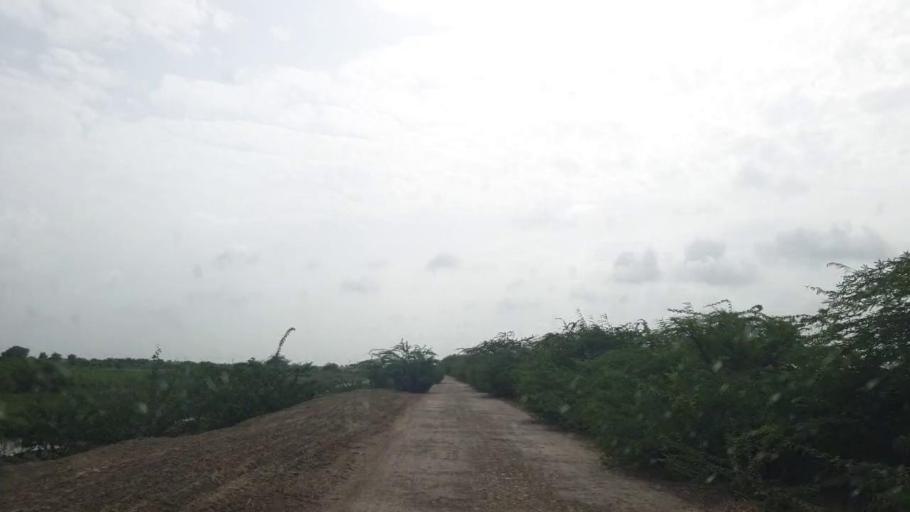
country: PK
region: Sindh
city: Tando Bago
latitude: 24.7973
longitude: 68.9946
